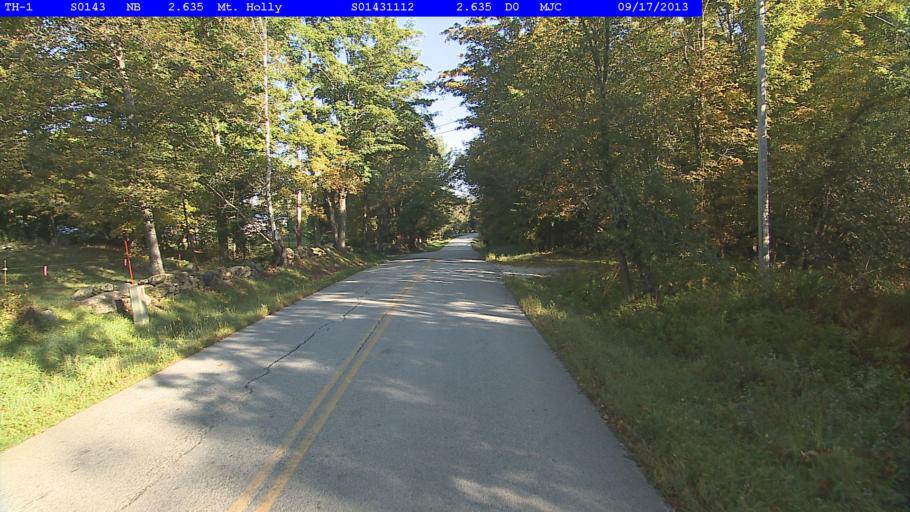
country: US
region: Vermont
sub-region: Rutland County
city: Rutland
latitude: 43.4356
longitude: -72.8264
